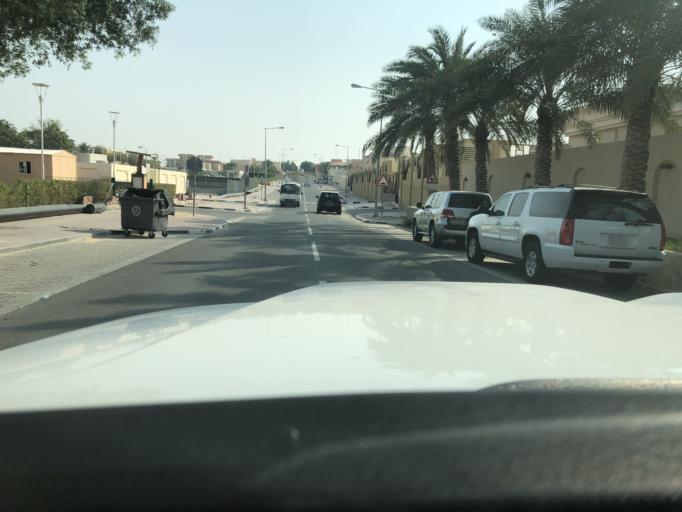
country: QA
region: Baladiyat ar Rayyan
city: Ar Rayyan
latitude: 25.3342
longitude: 51.4780
